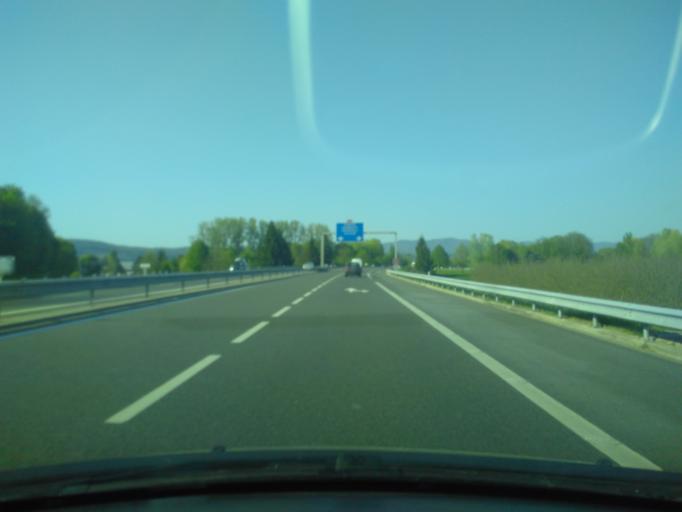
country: FR
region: Rhone-Alpes
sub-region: Departement de l'Isere
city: Saint-Quentin-sur-Isere
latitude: 45.2828
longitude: 5.5236
